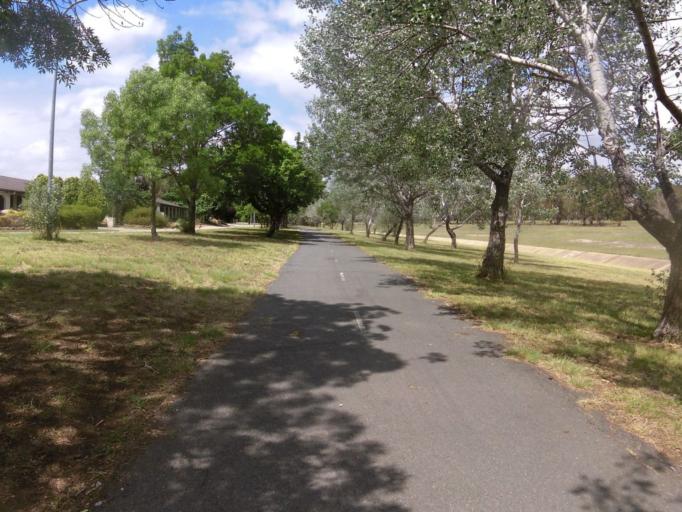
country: AU
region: Australian Capital Territory
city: Macarthur
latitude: -35.4178
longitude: 149.1098
